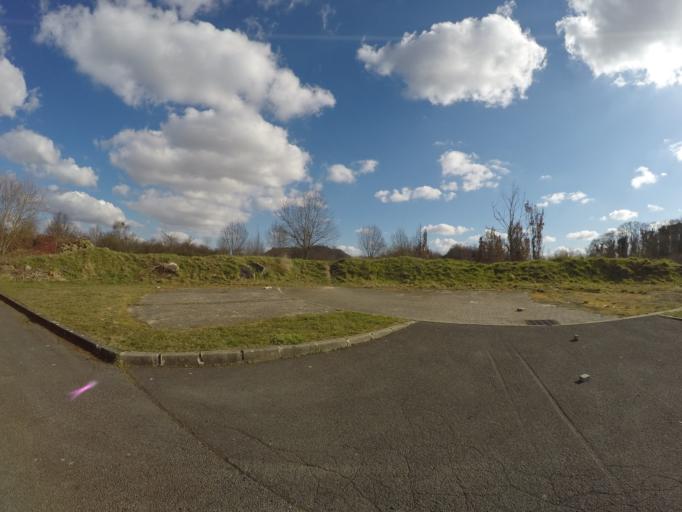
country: FR
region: Nord-Pas-de-Calais
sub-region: Departement du Pas-de-Calais
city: Bully-les-Mines
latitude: 50.4581
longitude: 2.7262
